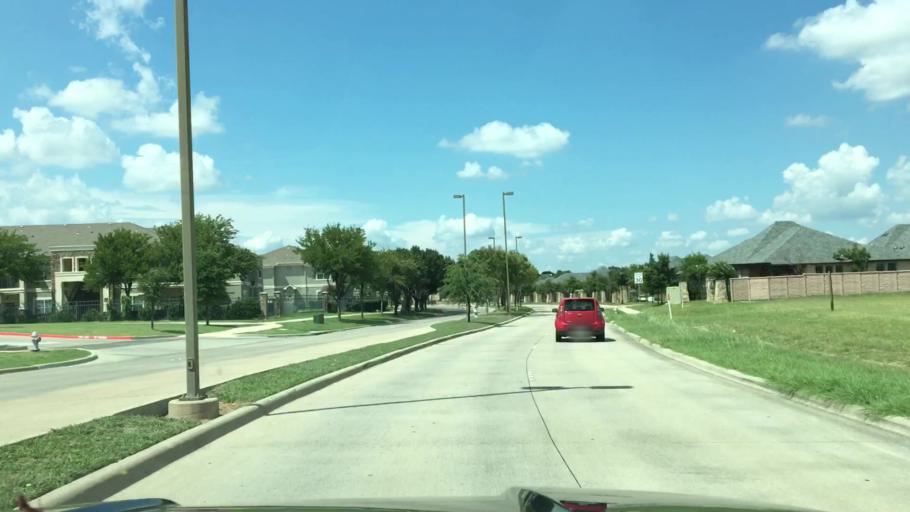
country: US
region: Texas
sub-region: Tarrant County
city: Keller
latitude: 32.9368
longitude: -97.2403
